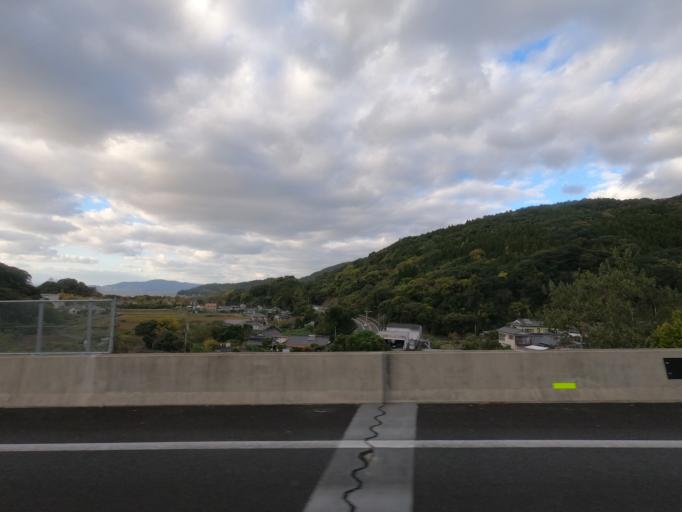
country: JP
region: Kumamoto
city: Minamata
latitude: 32.2282
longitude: 130.4418
